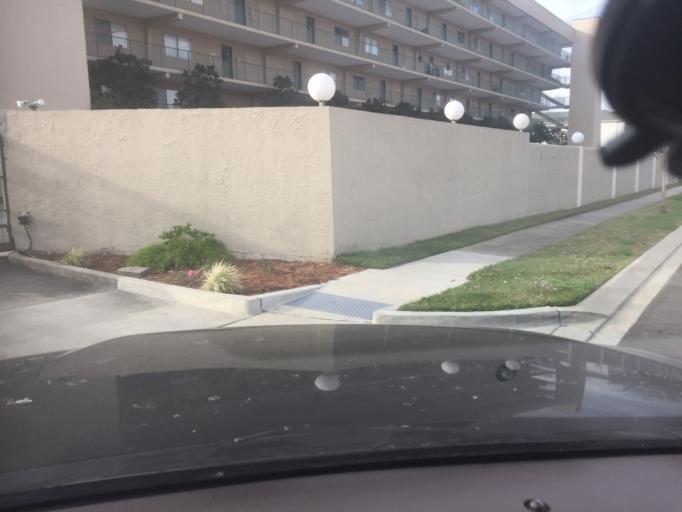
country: US
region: Louisiana
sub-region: Orleans Parish
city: New Orleans
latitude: 29.9976
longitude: -90.0843
